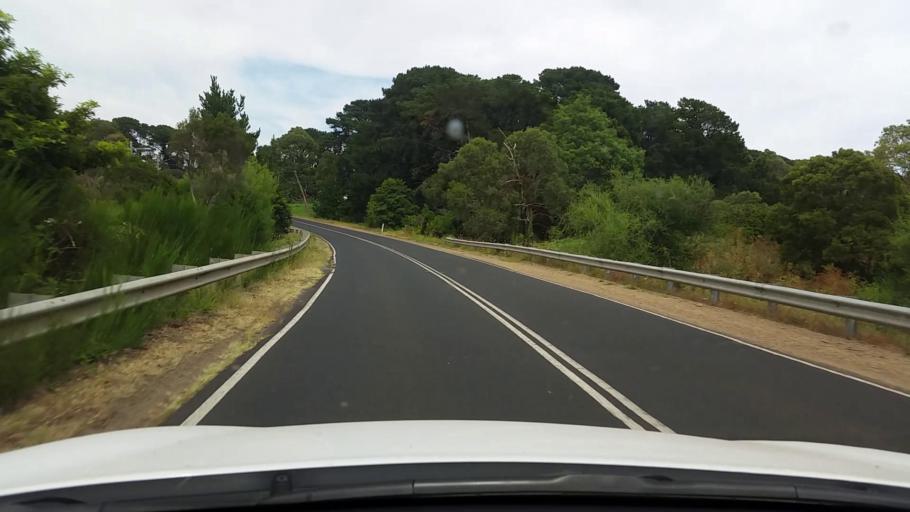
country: AU
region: Victoria
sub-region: Mornington Peninsula
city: Merricks
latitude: -38.4180
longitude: 145.0461
